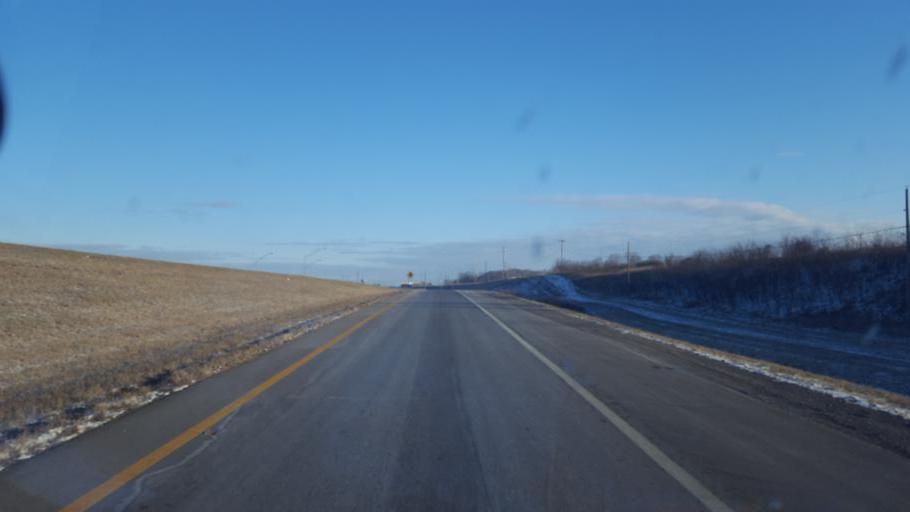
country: US
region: Ohio
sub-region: Pike County
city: Piketon
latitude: 39.0486
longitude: -83.0226
